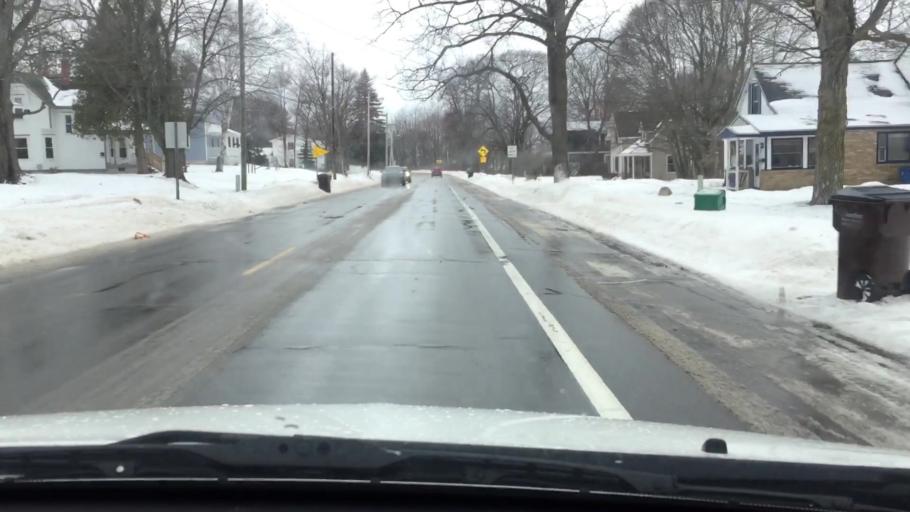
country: US
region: Michigan
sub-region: Wexford County
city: Cadillac
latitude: 44.2410
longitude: -85.4032
